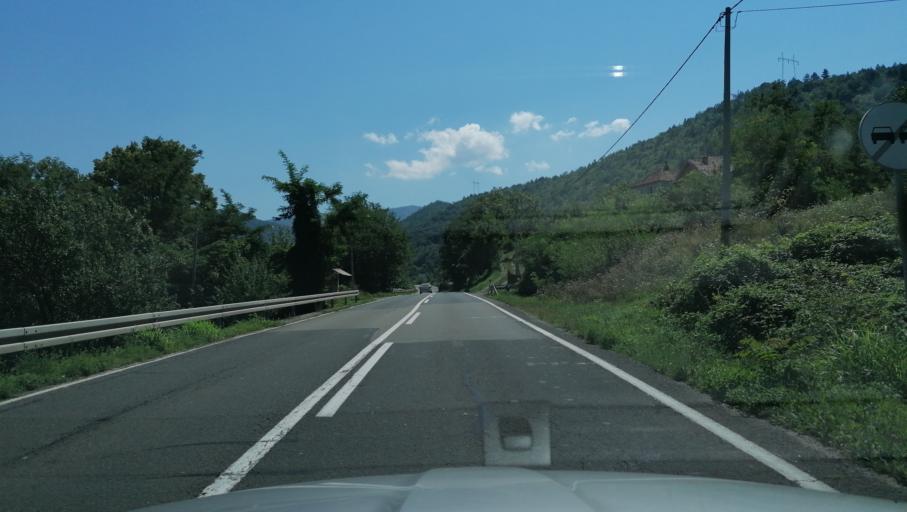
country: RS
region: Central Serbia
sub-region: Raski Okrug
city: Kraljevo
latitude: 43.6739
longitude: 20.5743
